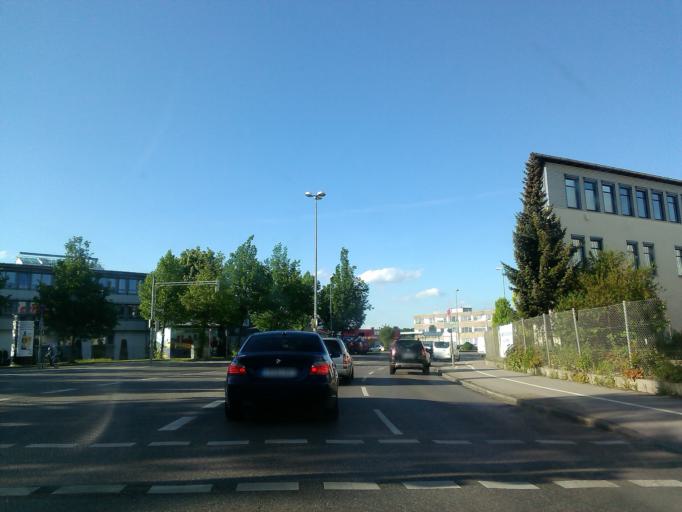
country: DE
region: Bavaria
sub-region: Swabia
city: Augsburg
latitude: 48.3797
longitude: 10.9289
